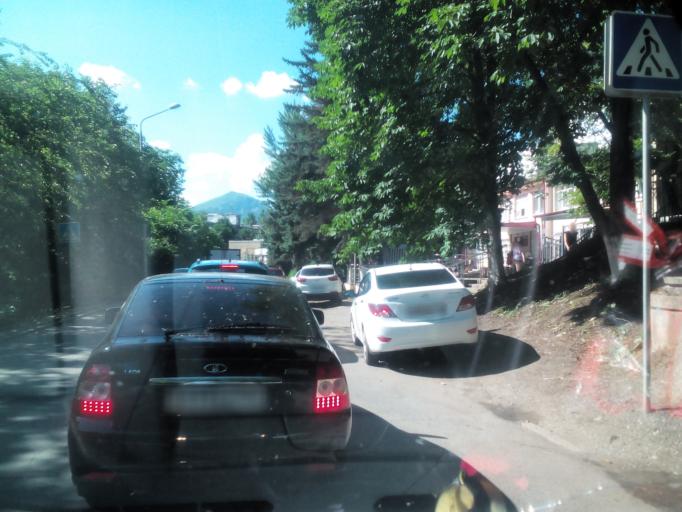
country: RU
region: Stavropol'skiy
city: Pyatigorsk
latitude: 44.0497
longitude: 43.0672
